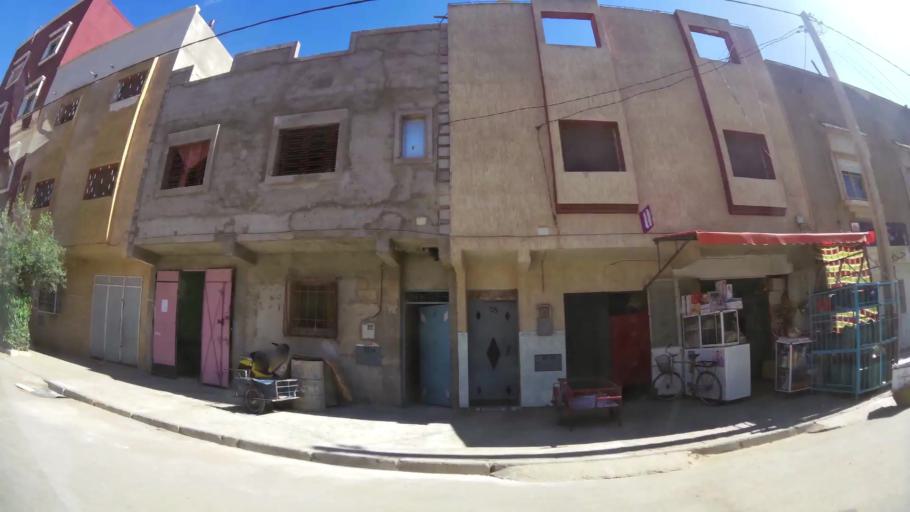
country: MA
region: Oriental
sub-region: Berkane-Taourirt
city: Berkane
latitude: 34.9387
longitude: -2.3384
